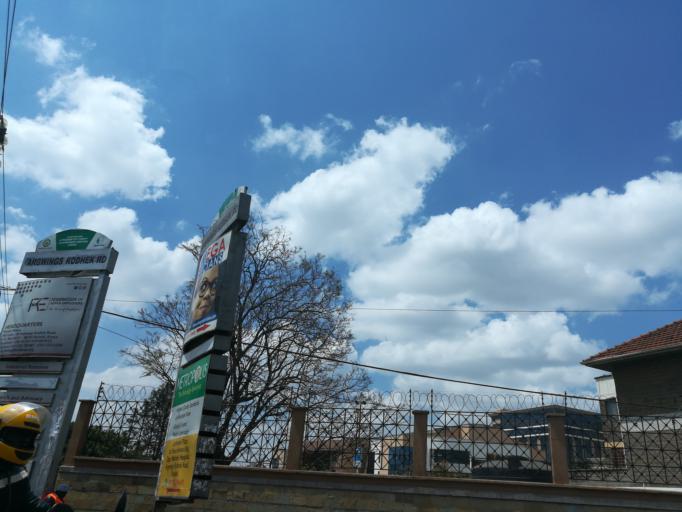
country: KE
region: Nairobi Area
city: Nairobi
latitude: -1.2953
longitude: 36.8026
